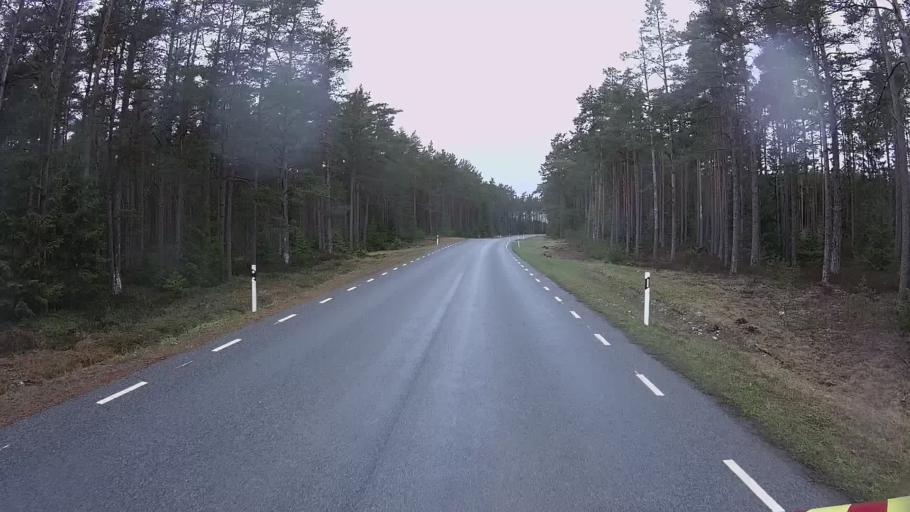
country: EE
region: Hiiumaa
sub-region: Kaerdla linn
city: Kardla
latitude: 58.9103
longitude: 22.3906
